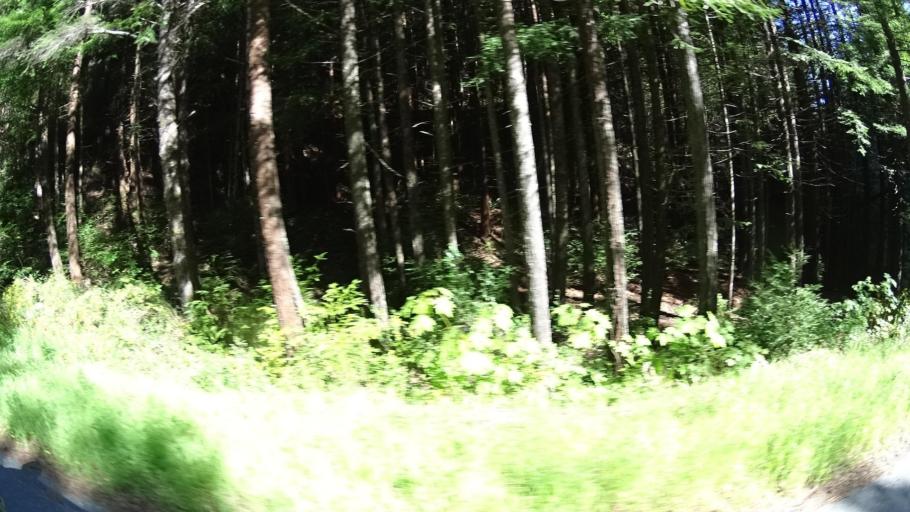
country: US
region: California
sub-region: Humboldt County
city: Rio Dell
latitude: 40.4647
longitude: -124.0534
